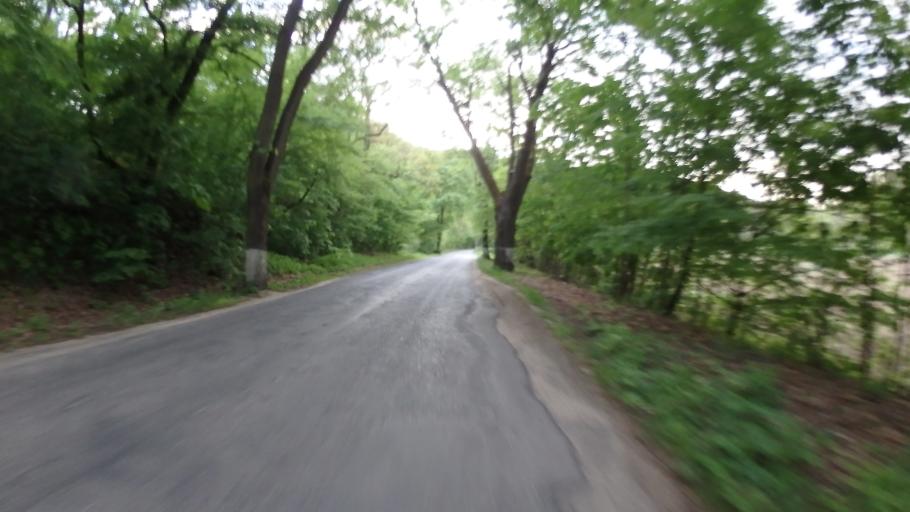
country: CZ
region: South Moravian
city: Strelice
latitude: 49.1384
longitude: 16.4674
